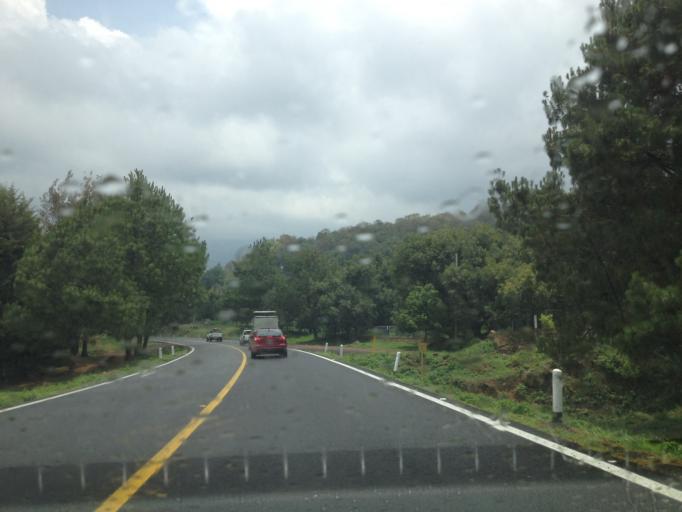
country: MX
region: Michoacan
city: Tingambato
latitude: 19.5003
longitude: -101.8404
